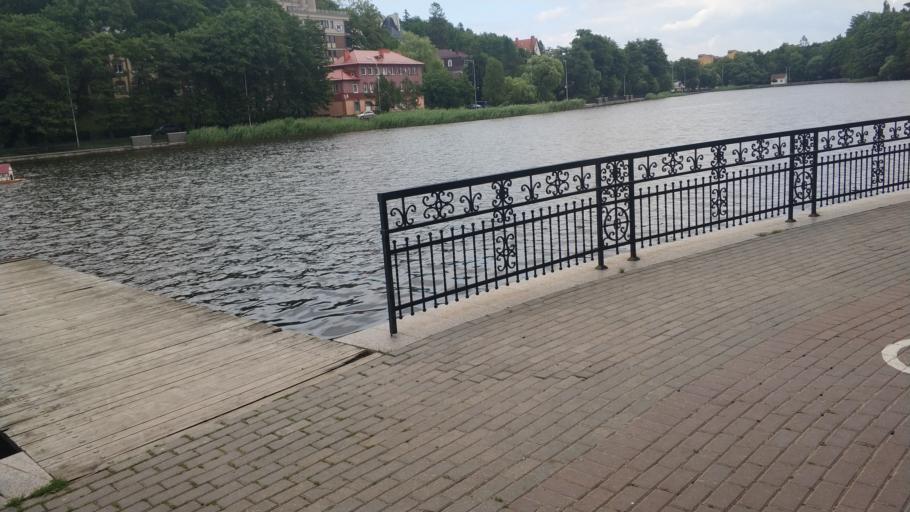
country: RU
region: Kaliningrad
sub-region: Gorod Svetlogorsk
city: Svetlogorsk
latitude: 54.9371
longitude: 20.1545
